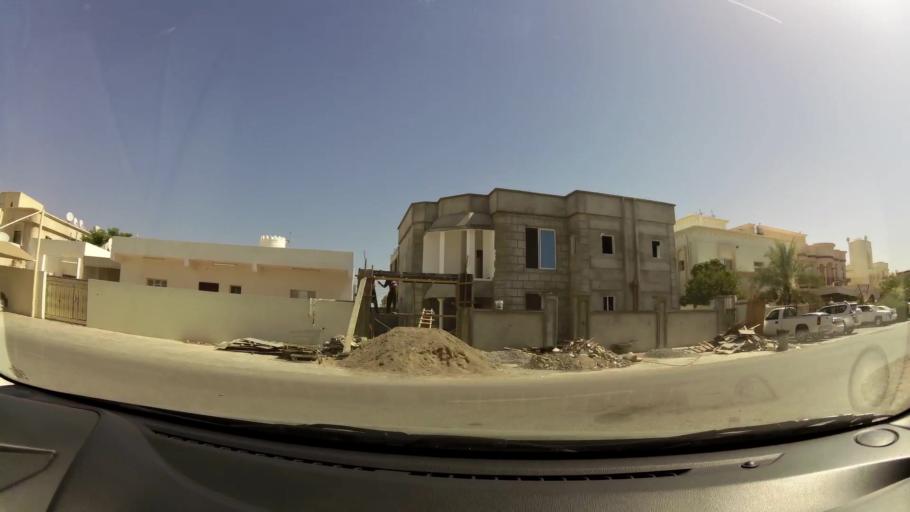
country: OM
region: Muhafazat Masqat
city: As Sib al Jadidah
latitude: 23.6029
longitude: 58.2437
